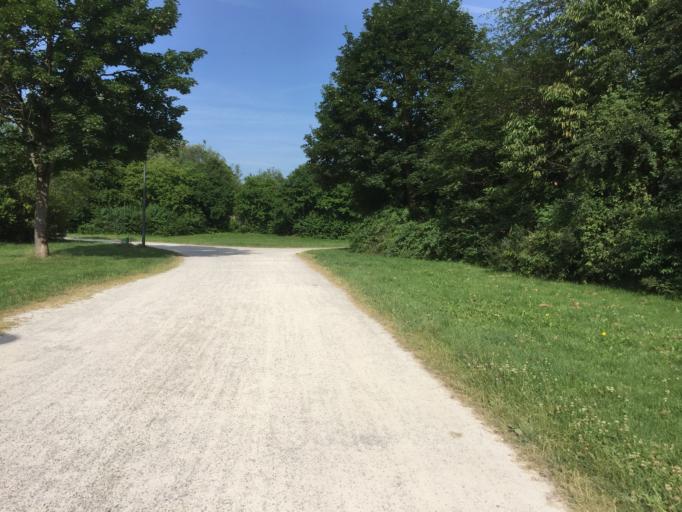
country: DE
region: Bavaria
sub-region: Upper Bavaria
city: Bogenhausen
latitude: 48.1232
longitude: 11.6365
